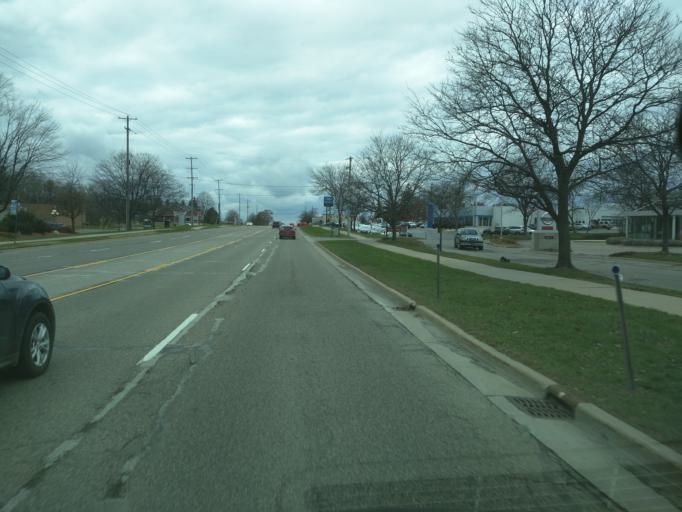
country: US
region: Michigan
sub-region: Ingham County
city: Okemos
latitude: 42.7182
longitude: -84.4112
